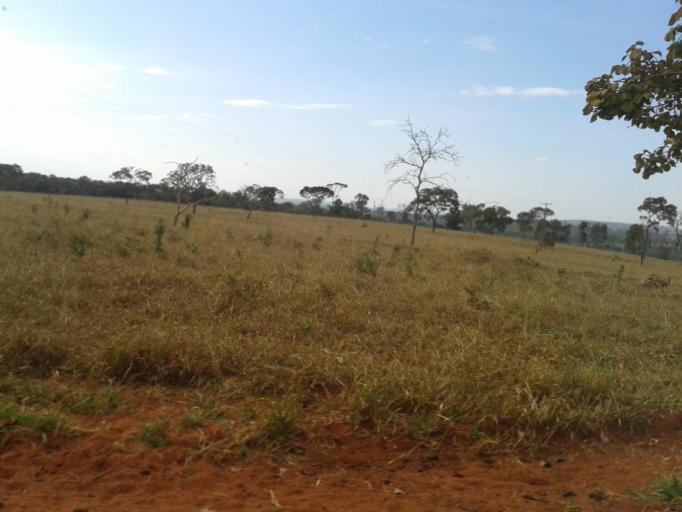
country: BR
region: Minas Gerais
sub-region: Ituiutaba
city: Ituiutaba
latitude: -19.0715
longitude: -49.3640
